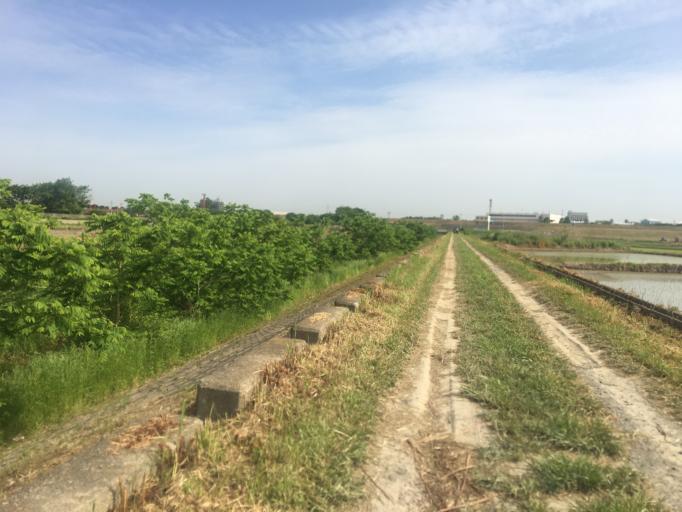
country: JP
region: Saitama
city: Shiki
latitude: 35.8515
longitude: 139.6032
